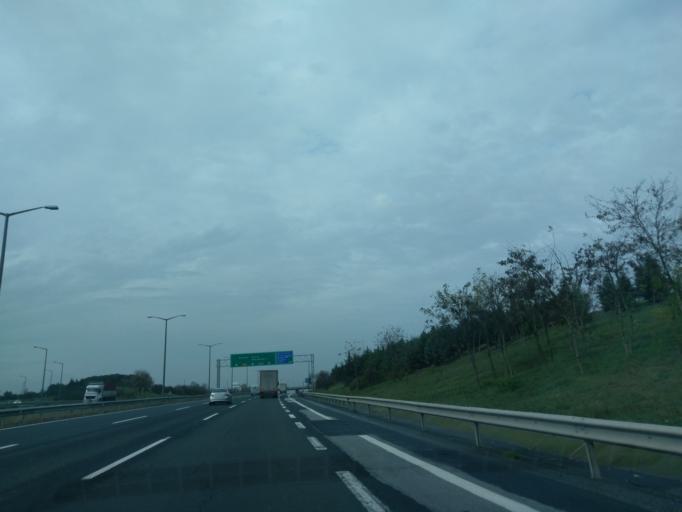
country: TR
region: Istanbul
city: Buyukcavuslu
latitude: 41.1911
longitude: 28.0904
